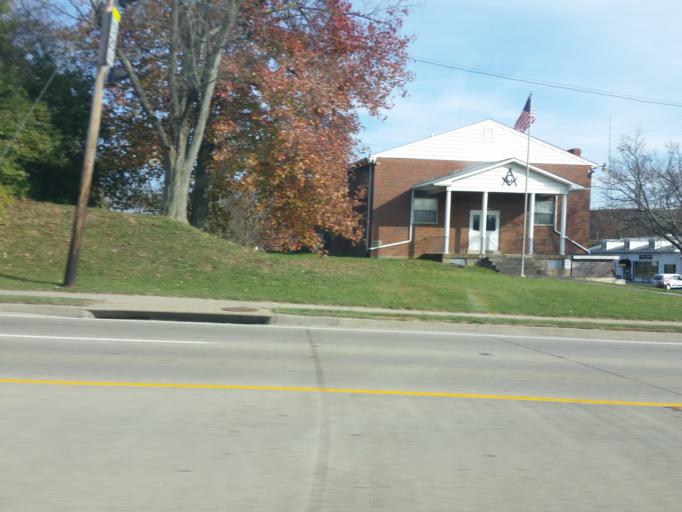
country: US
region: Kentucky
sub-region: Campbell County
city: Alexandria
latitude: 38.9620
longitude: -84.3929
